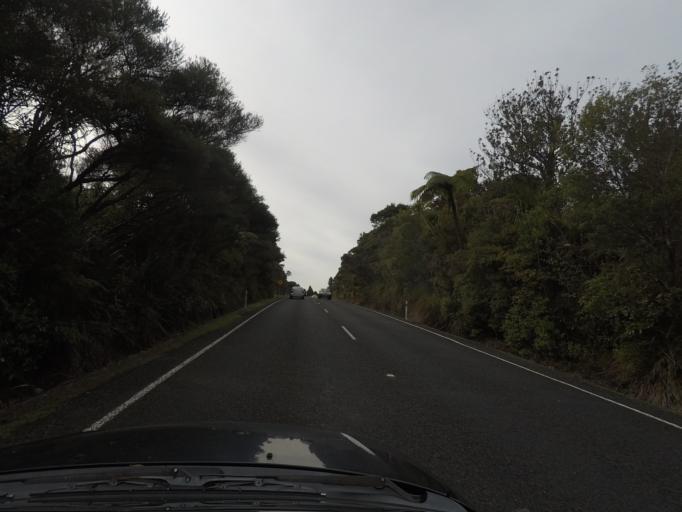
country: NZ
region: Auckland
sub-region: Auckland
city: Titirangi
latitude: -36.9468
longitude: 174.5249
